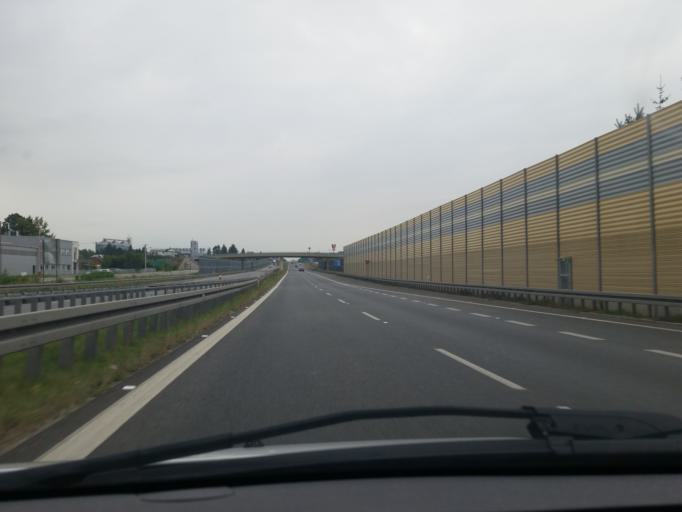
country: PL
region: Masovian Voivodeship
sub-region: Powiat zyrardowski
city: Radziejowice
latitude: 51.9987
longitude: 20.5540
